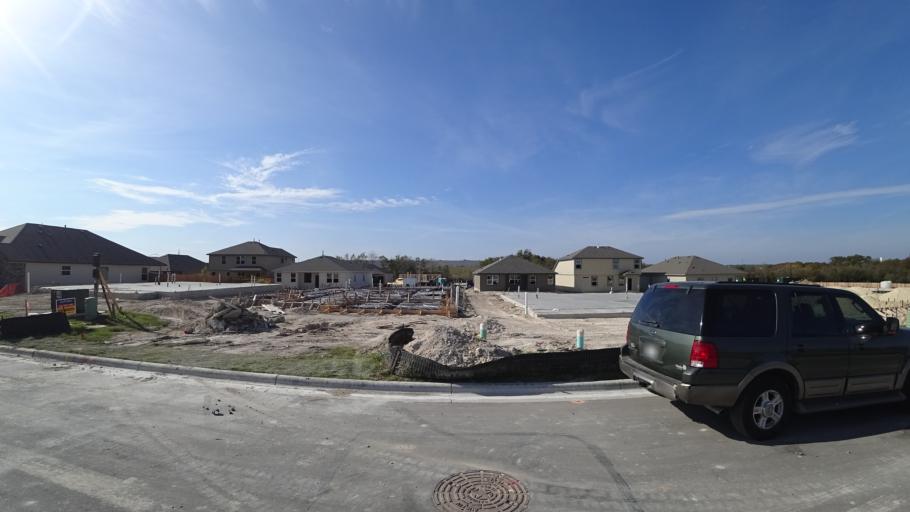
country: US
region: Texas
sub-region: Travis County
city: Pflugerville
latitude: 30.4103
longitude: -97.6400
